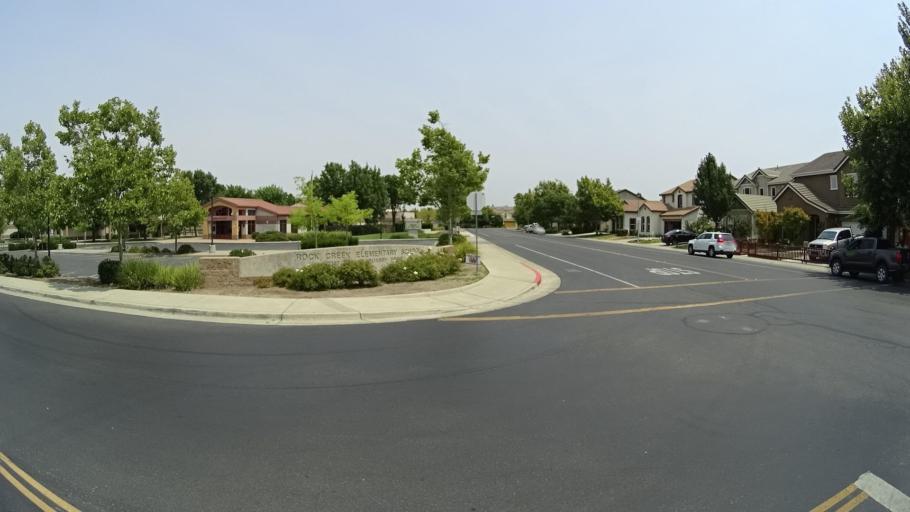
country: US
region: California
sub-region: Placer County
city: Rocklin
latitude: 38.7977
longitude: -121.2802
